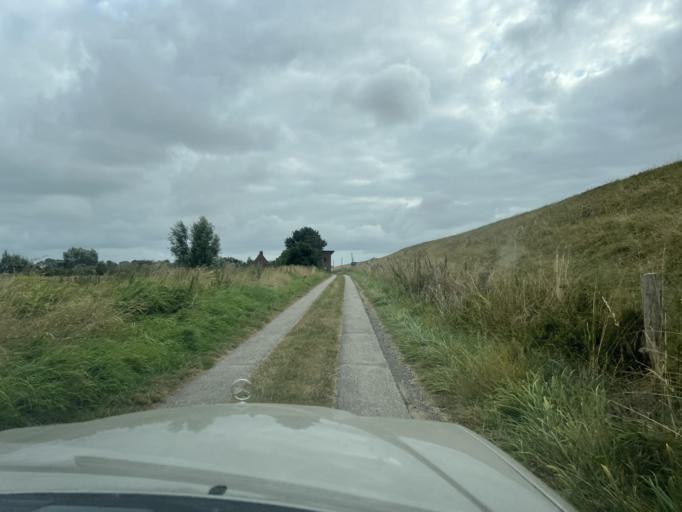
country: DE
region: Schleswig-Holstein
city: Groven
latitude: 54.3235
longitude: 8.9852
